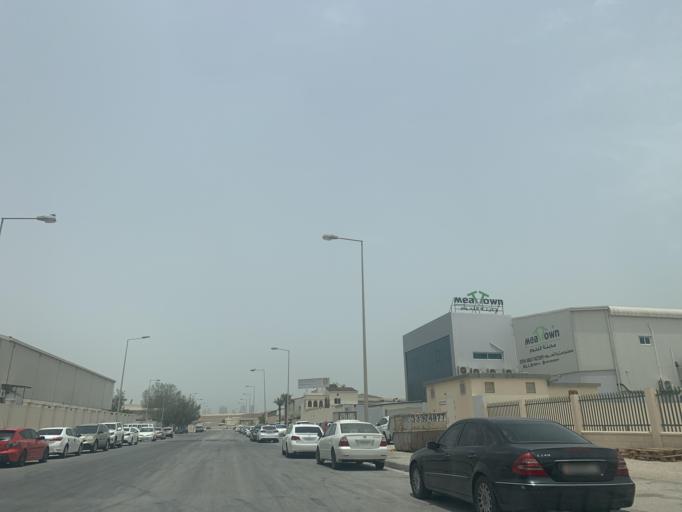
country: BH
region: Northern
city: Sitrah
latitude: 26.1798
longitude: 50.6098
